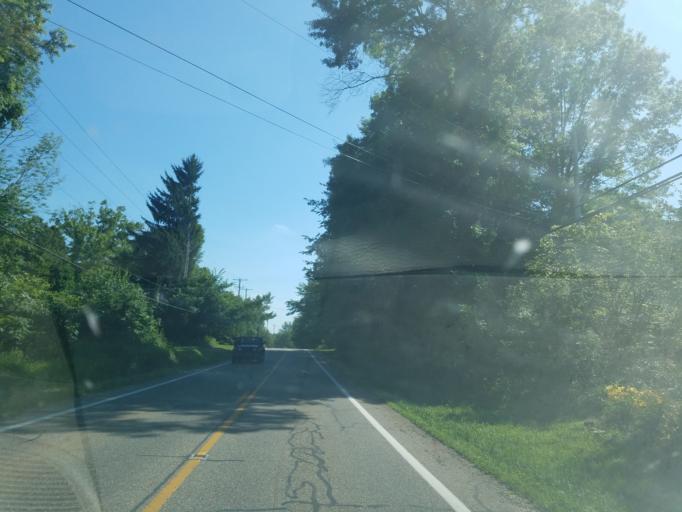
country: US
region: Ohio
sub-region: Portage County
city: Ravenna
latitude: 41.2172
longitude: -81.2408
